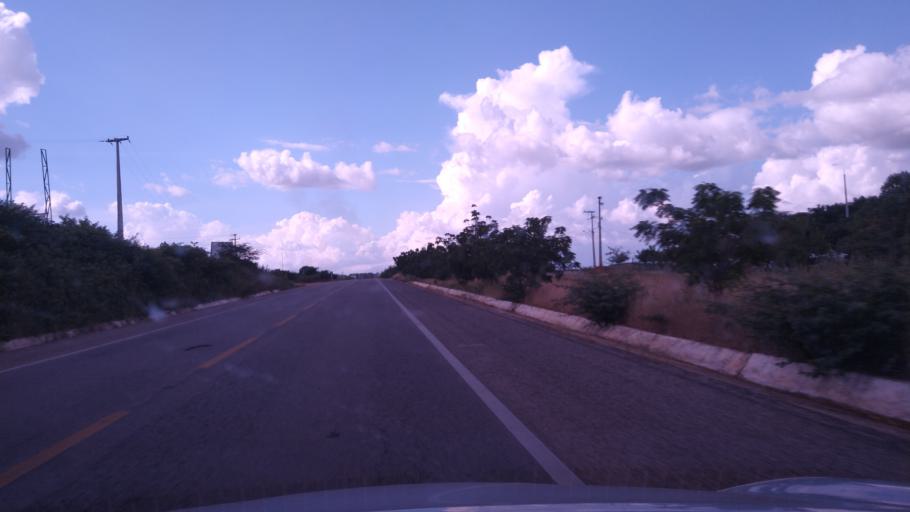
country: BR
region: Ceara
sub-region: Caninde
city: Caninde
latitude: -4.3907
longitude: -39.3135
